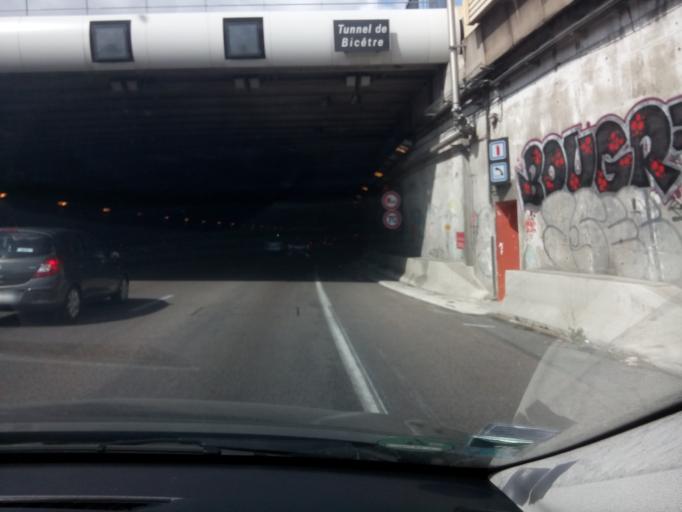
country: FR
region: Ile-de-France
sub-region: Departement du Val-de-Marne
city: Cachan
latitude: 48.8017
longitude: 2.3436
